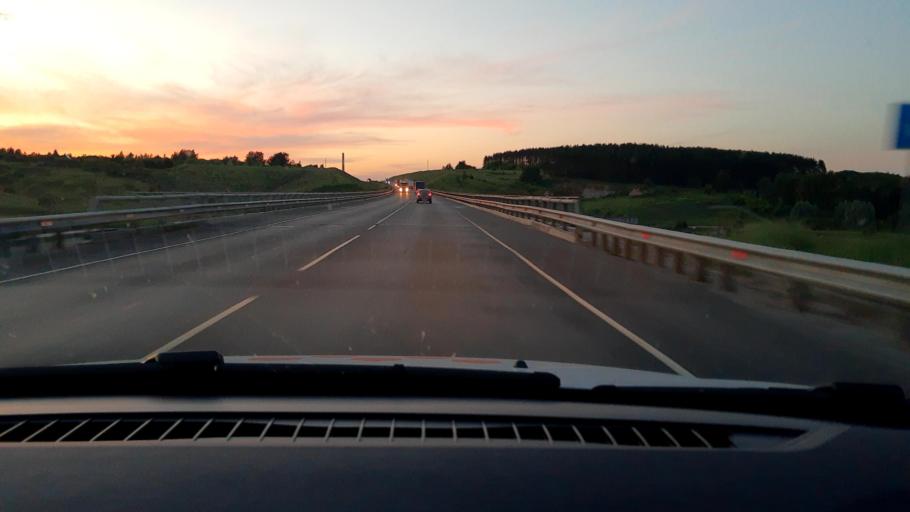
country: RU
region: Nizjnij Novgorod
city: Kstovo
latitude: 56.0772
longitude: 44.1334
